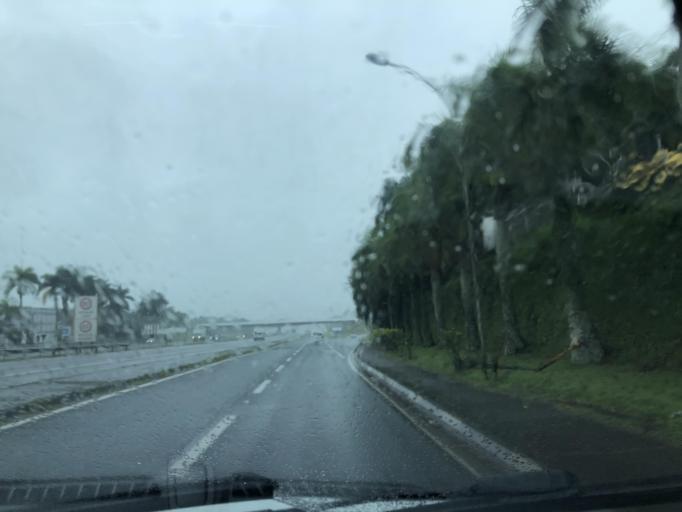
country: BR
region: Sao Paulo
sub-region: Registro
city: Registro
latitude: -24.5051
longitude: -47.8483
